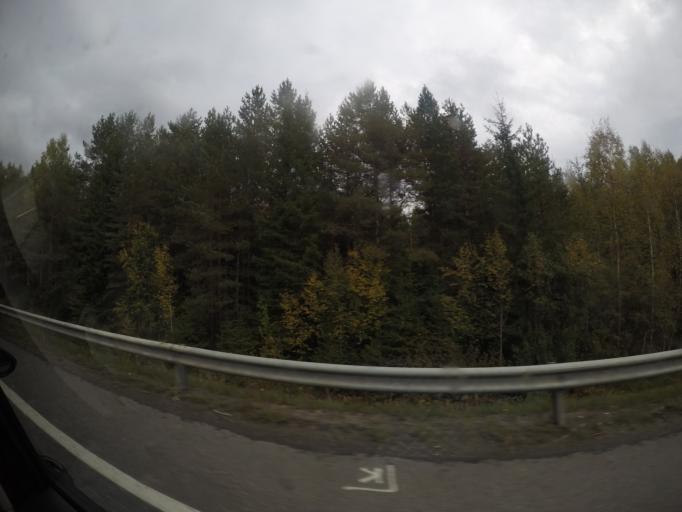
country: FI
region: Haeme
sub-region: Haemeenlinna
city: Parola
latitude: 61.1533
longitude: 24.4117
